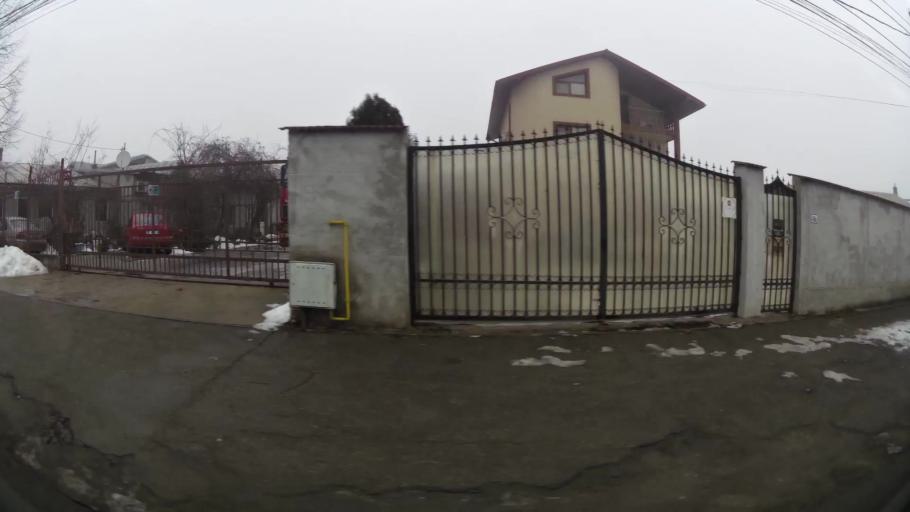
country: RO
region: Ilfov
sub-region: Comuna Chiajna
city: Rosu
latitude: 44.4680
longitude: 26.0098
